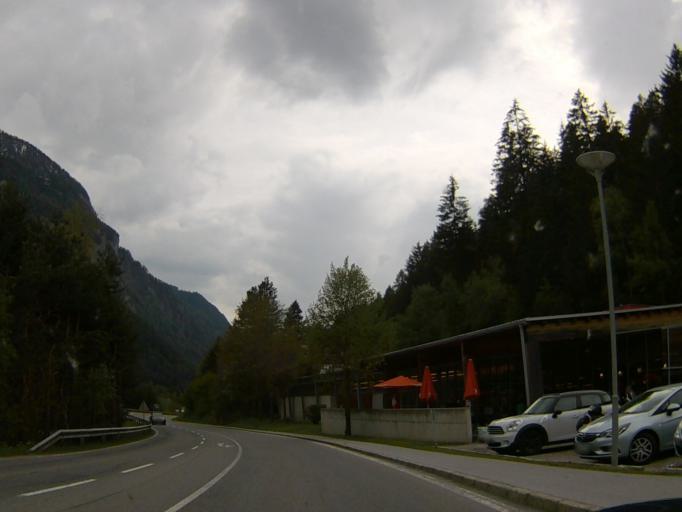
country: AT
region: Tyrol
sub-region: Politischer Bezirk Landeck
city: Pfunds
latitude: 46.9681
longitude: 10.5304
